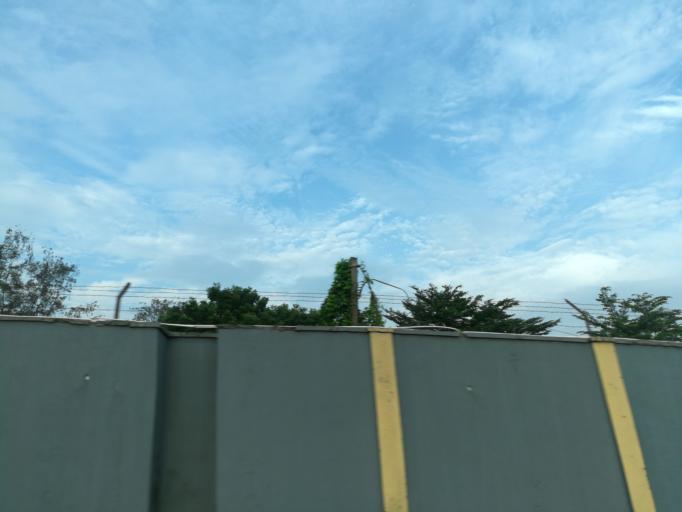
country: NG
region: Lagos
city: Ikeja
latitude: 6.5816
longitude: 3.3340
